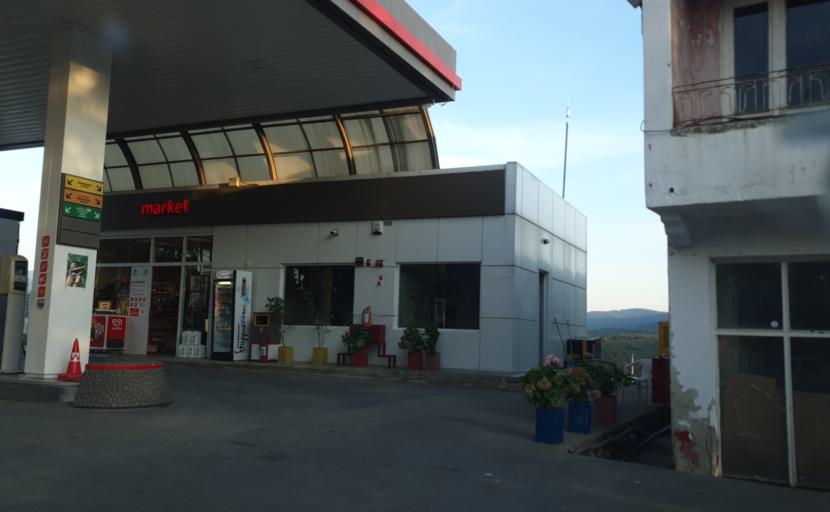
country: TR
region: Kirklareli
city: Sergen
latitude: 41.8221
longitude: 27.7618
